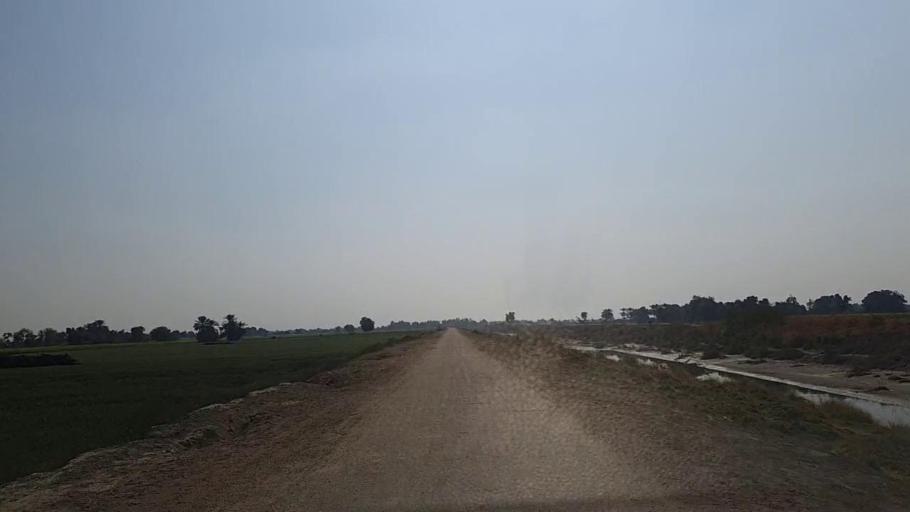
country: PK
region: Sindh
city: Nawabshah
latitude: 26.2582
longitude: 68.5030
